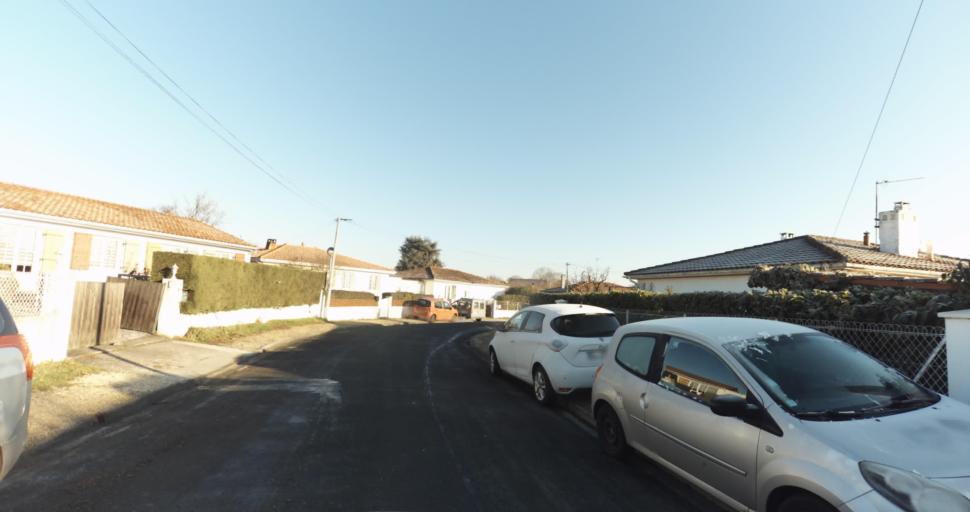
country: FR
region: Aquitaine
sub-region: Departement de la Gironde
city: Carbon-Blanc
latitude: 44.9040
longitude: -0.5009
